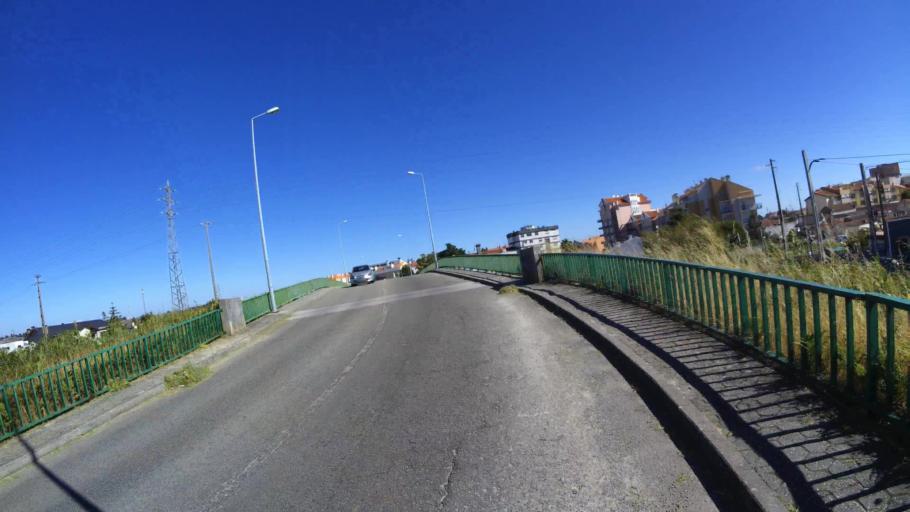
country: PT
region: Aveiro
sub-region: Aveiro
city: Aveiro
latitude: 40.6561
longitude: -8.6236
